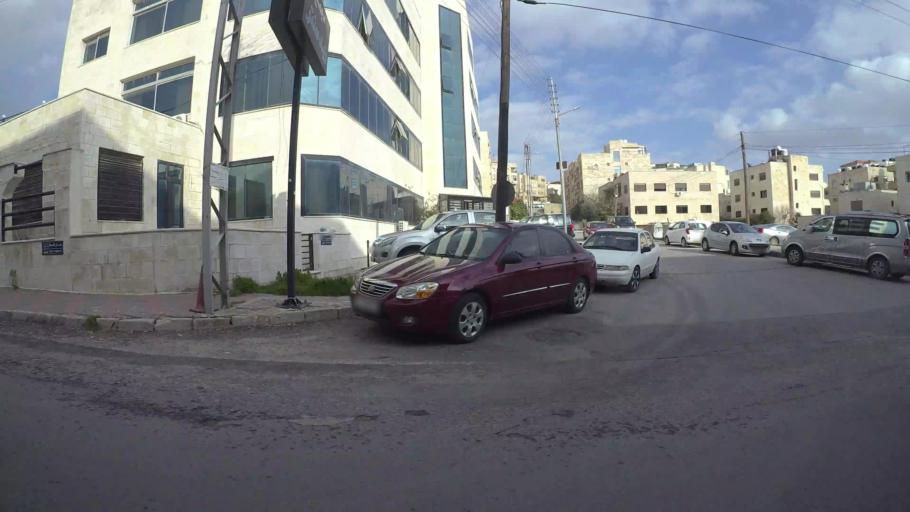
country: JO
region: Amman
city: Wadi as Sir
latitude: 31.9776
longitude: 35.8446
